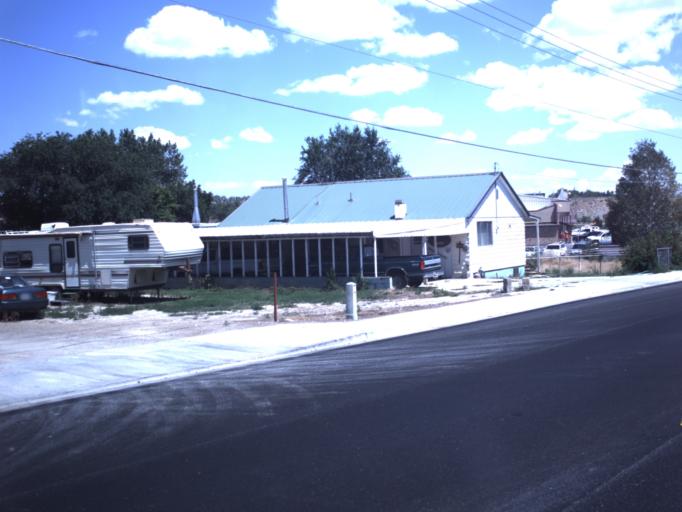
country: US
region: Utah
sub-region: Emery County
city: Orangeville
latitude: 39.2312
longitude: -111.0482
